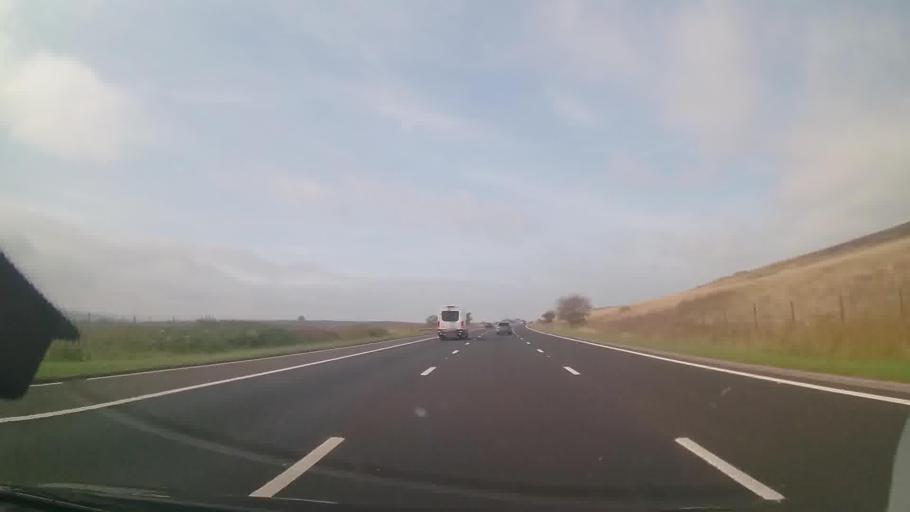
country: GB
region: England
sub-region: Cumbria
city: Appleby-in-Westmorland
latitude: 54.4877
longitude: -2.6402
